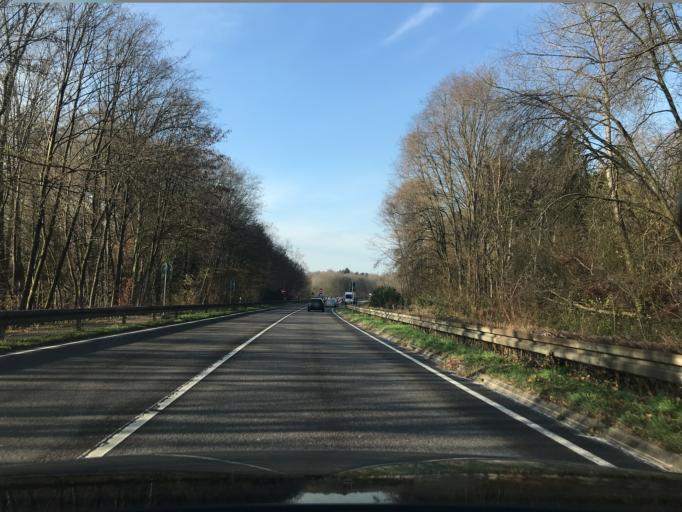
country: DE
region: North Rhine-Westphalia
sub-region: Regierungsbezirk Dusseldorf
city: Solingen
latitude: 51.1856
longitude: 7.1171
